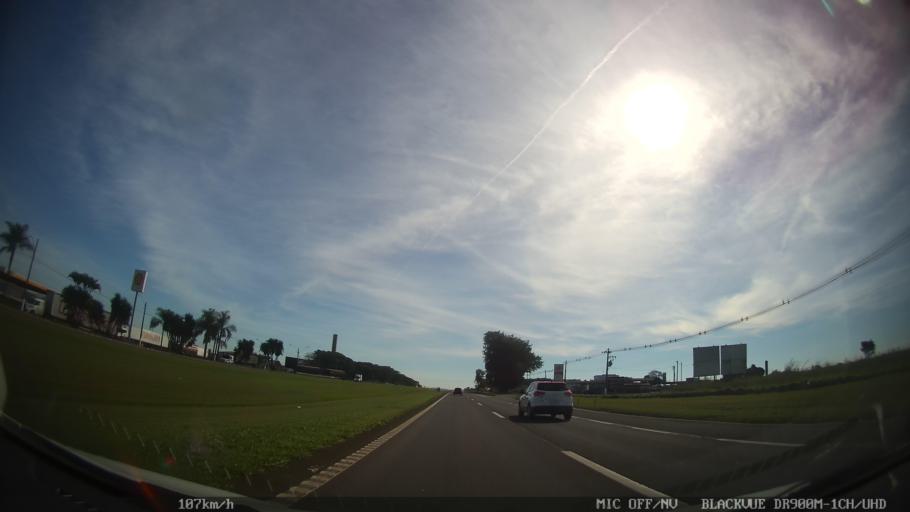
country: BR
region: Sao Paulo
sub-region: Araras
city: Araras
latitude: -22.4121
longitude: -47.3898
